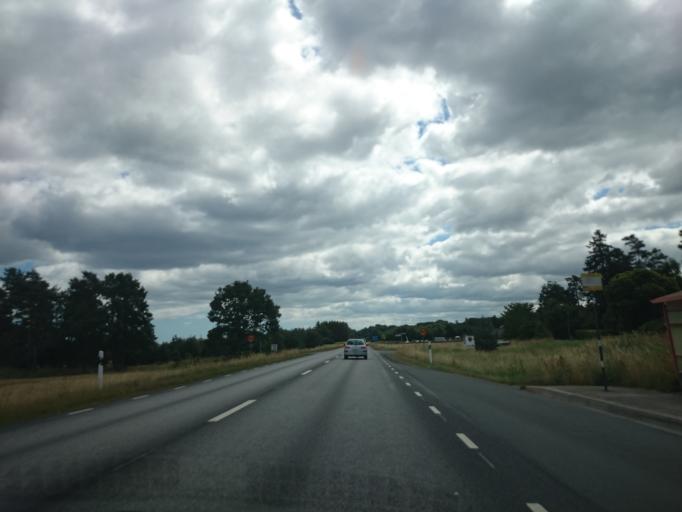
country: SE
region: Skane
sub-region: Kristianstads Kommun
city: Degeberga
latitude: 55.8104
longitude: 14.1394
